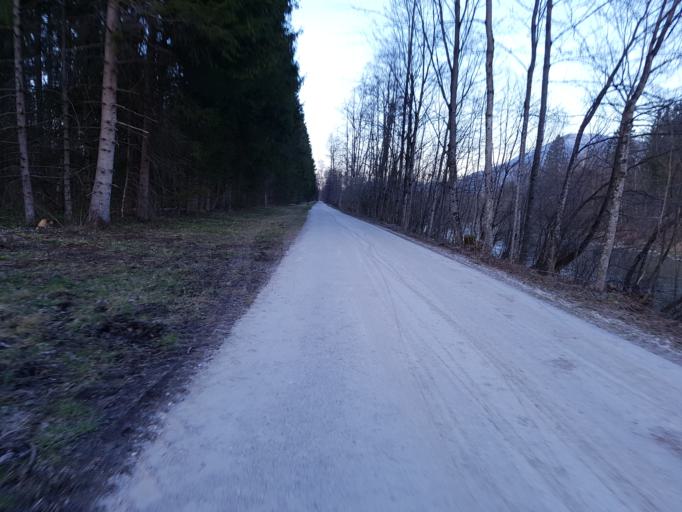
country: AT
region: Salzburg
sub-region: Politischer Bezirk Salzburg-Umgebung
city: Elsbethen
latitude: 47.7468
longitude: 13.0802
